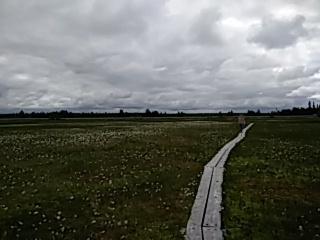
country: FI
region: Lapland
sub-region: Pohjois-Lappi
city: Sodankylae
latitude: 67.7075
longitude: 26.7504
